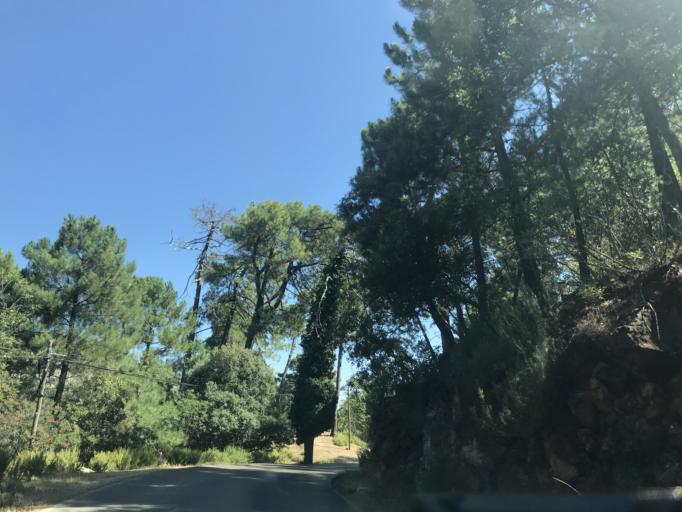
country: ES
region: Andalusia
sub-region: Provincia de Jaen
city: La Iruela
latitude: 37.9205
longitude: -2.9453
